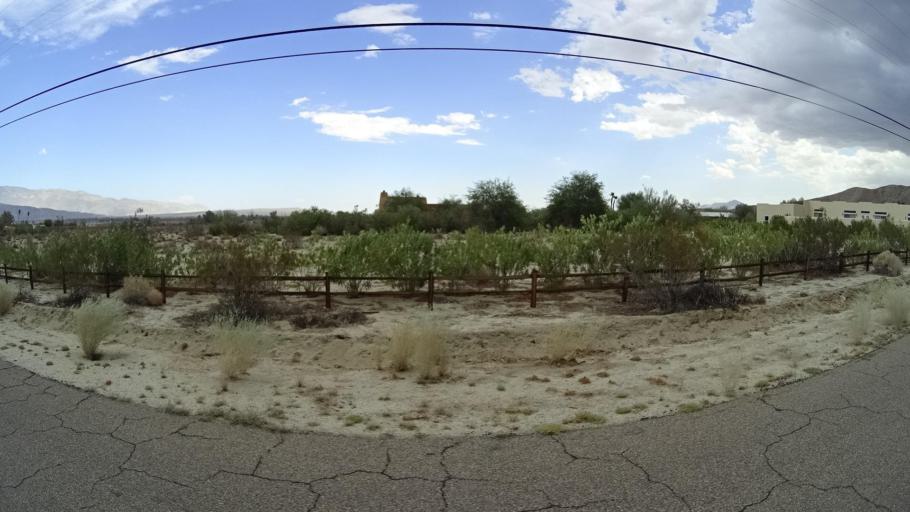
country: US
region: California
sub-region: San Diego County
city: Borrego Springs
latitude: 33.2599
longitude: -116.3914
